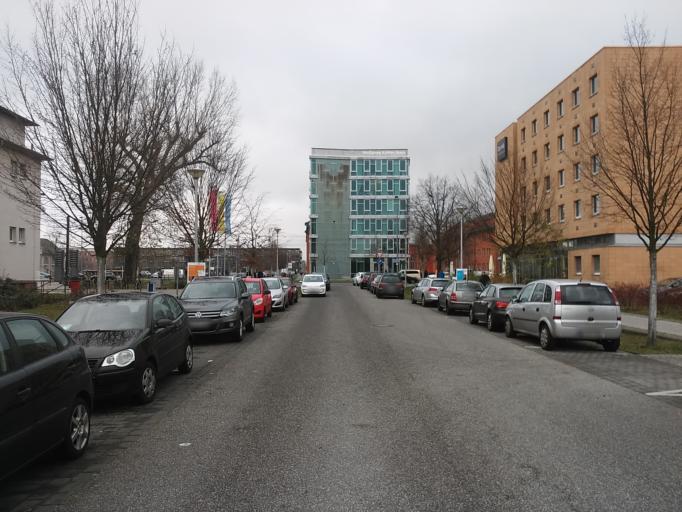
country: DE
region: Berlin
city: Adlershof
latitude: 52.4310
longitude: 13.5350
